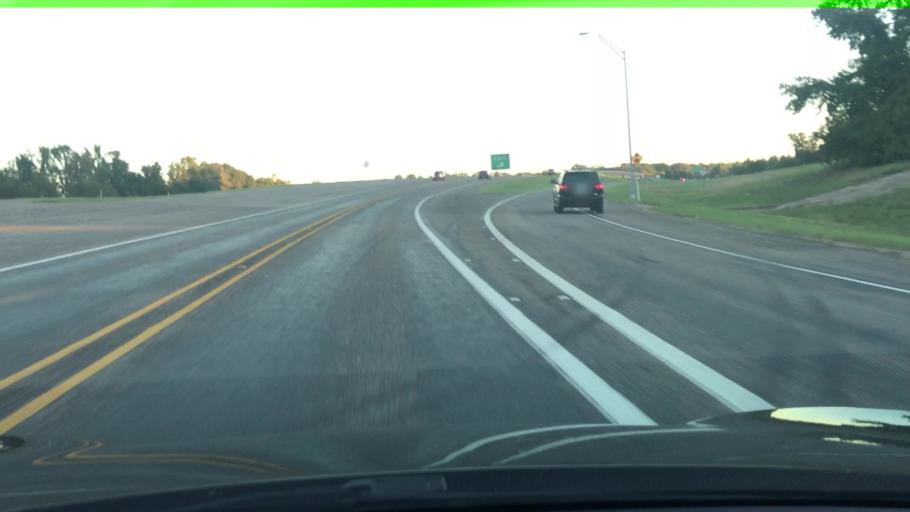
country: US
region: Texas
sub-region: Henderson County
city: Athens
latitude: 32.1863
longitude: -95.8144
